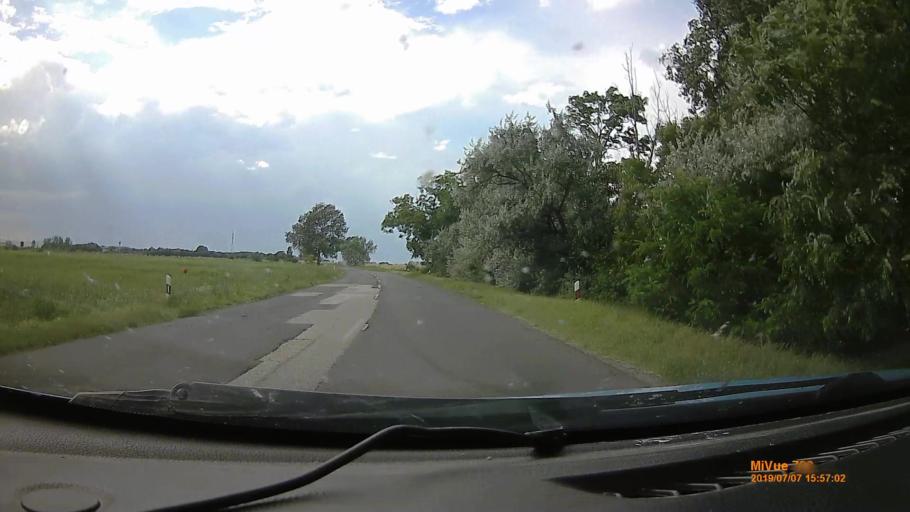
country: HU
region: Pest
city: Szentlorinckata
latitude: 47.5737
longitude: 19.7669
